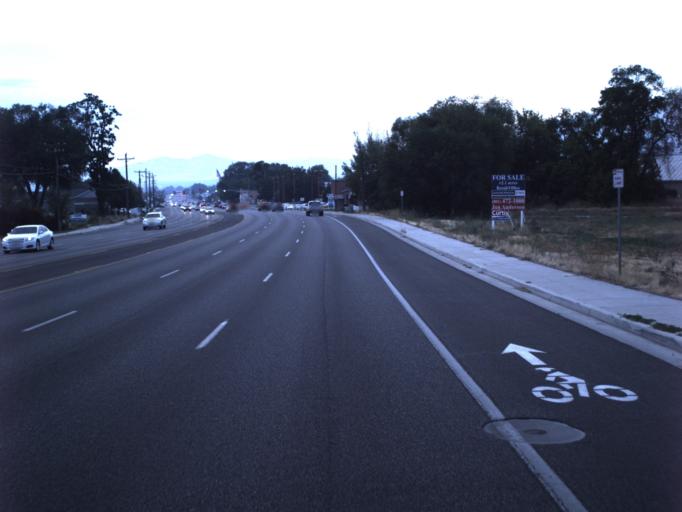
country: US
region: Utah
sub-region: Utah County
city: Lindon
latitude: 40.3422
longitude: -111.7203
